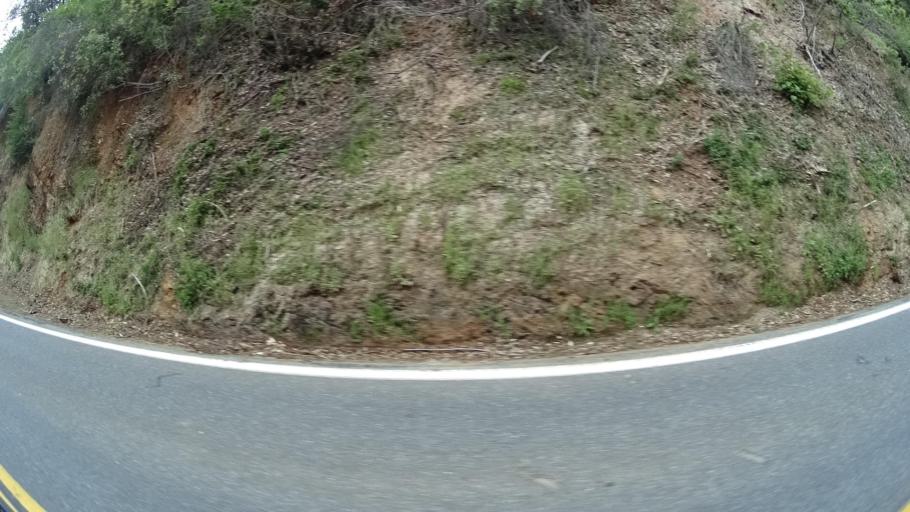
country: US
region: California
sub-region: Humboldt County
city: Willow Creek
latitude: 41.0095
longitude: -123.6379
